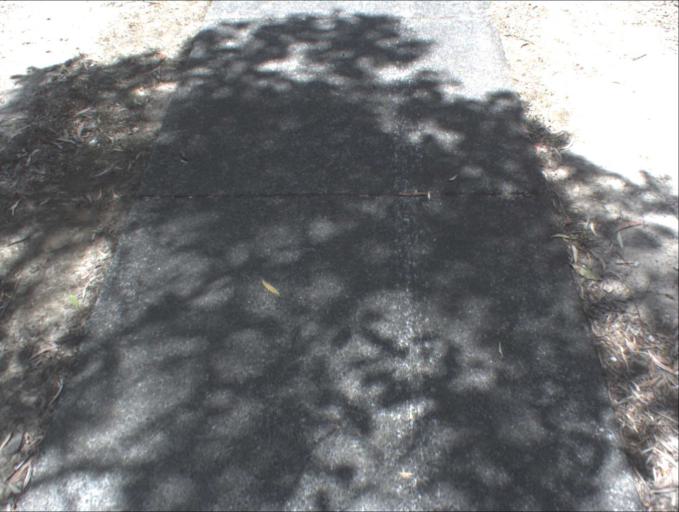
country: AU
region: Queensland
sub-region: Logan
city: Slacks Creek
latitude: -27.6415
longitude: 153.1740
